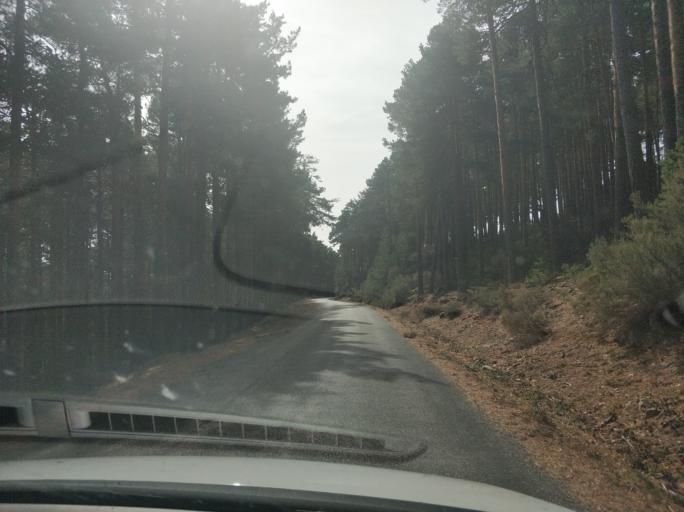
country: ES
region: Castille and Leon
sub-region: Provincia de Soria
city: Duruelo de la Sierra
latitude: 41.9905
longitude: -2.9223
